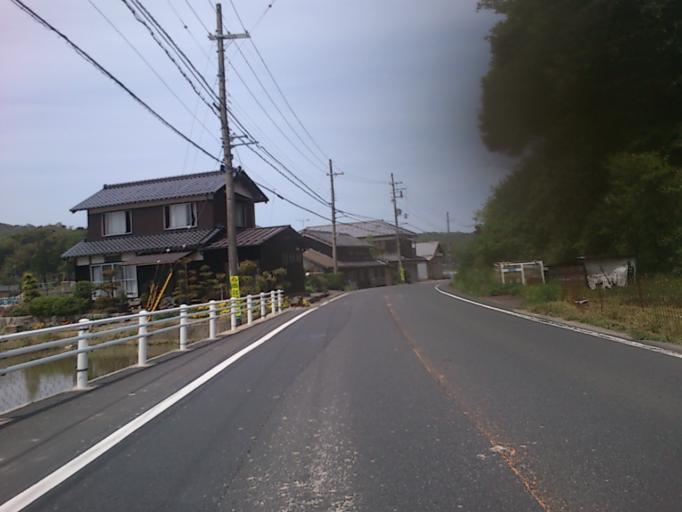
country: JP
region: Kyoto
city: Miyazu
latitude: 35.6871
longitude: 135.0980
